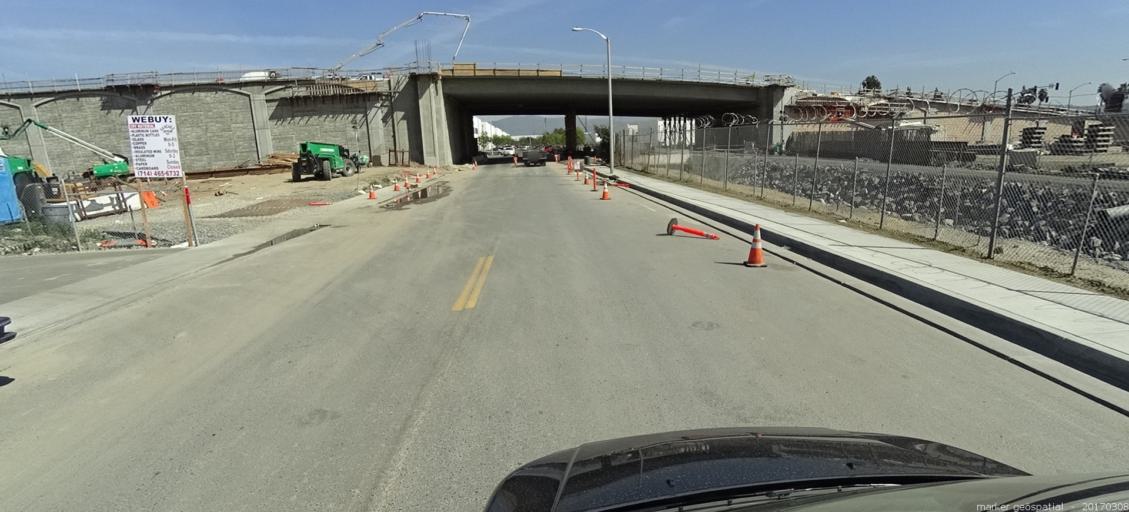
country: US
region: California
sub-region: Orange County
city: Yorba Linda
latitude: 33.8658
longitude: -117.8194
